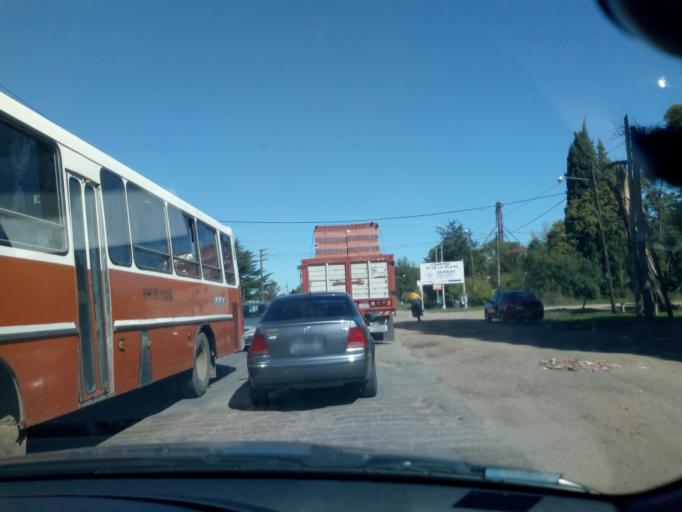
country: AR
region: Buenos Aires
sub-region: Partido de La Plata
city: La Plata
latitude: -34.9991
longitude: -58.0152
